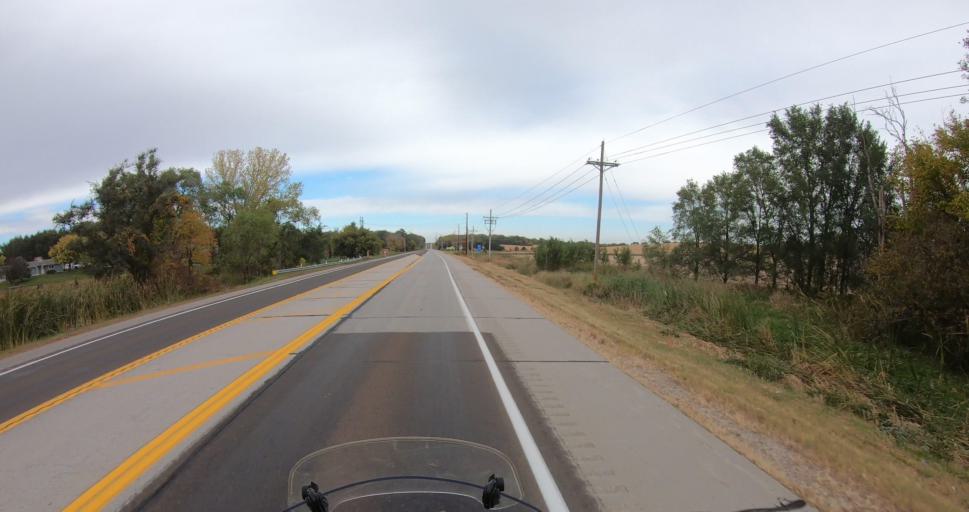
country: US
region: Nebraska
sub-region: Dodge County
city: Fremont
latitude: 41.3766
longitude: -96.5019
